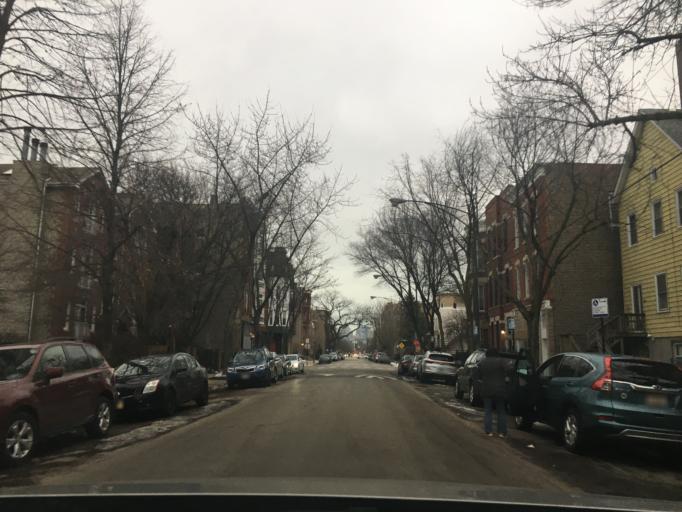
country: US
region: Illinois
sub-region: Cook County
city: Chicago
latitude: 41.8934
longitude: -87.6649
